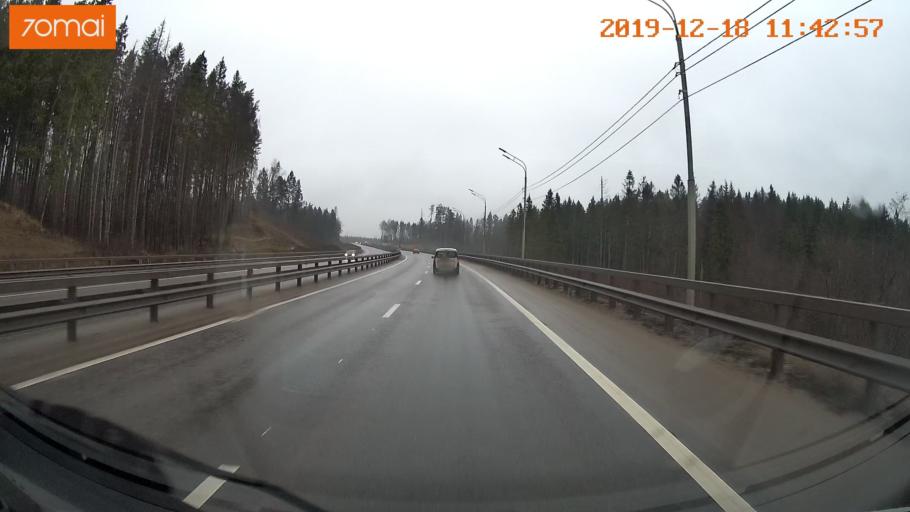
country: RU
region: Moskovskaya
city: Zvenigorod
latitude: 55.7294
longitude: 36.8798
